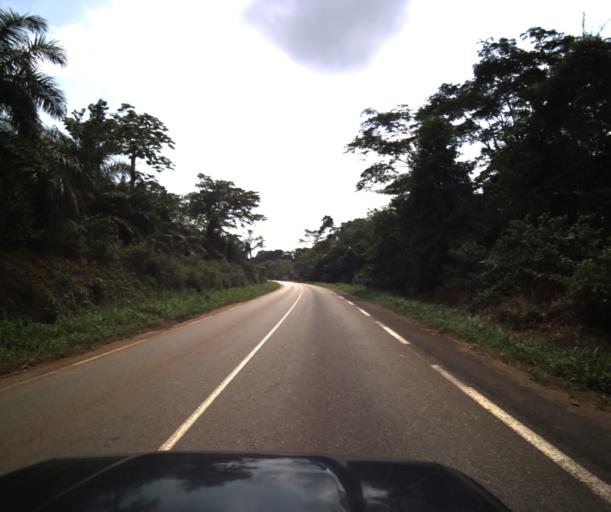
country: CM
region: Centre
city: Eseka
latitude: 3.8708
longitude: 10.6360
